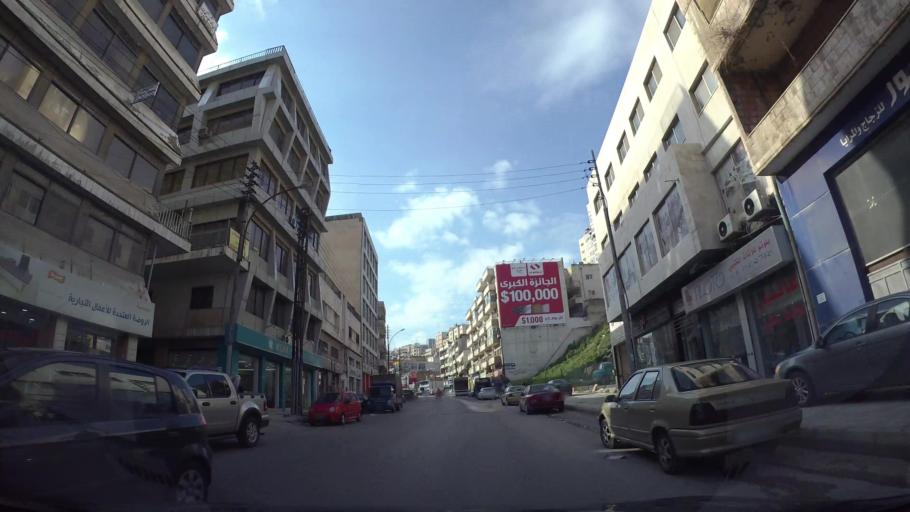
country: JO
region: Amman
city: Amman
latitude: 31.9557
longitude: 35.9155
